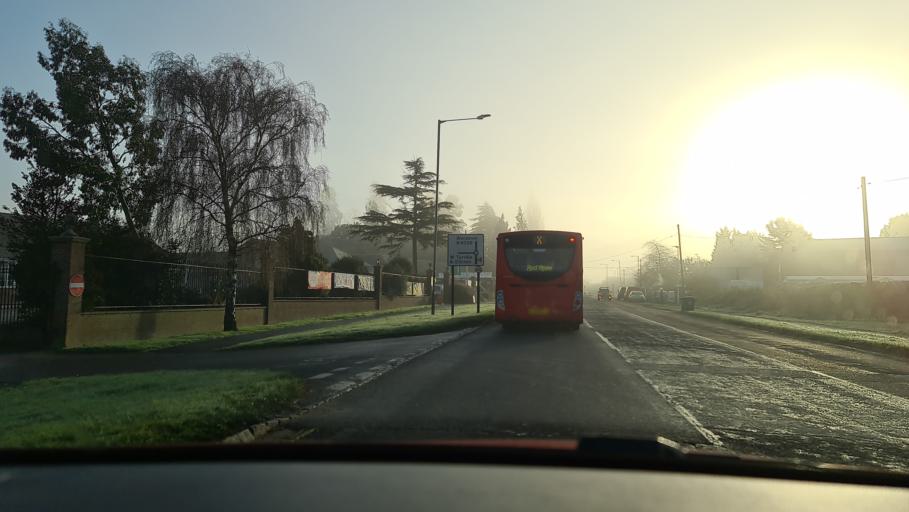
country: GB
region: England
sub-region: Buckinghamshire
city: Weston Turville
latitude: 51.7759
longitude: -0.7579
